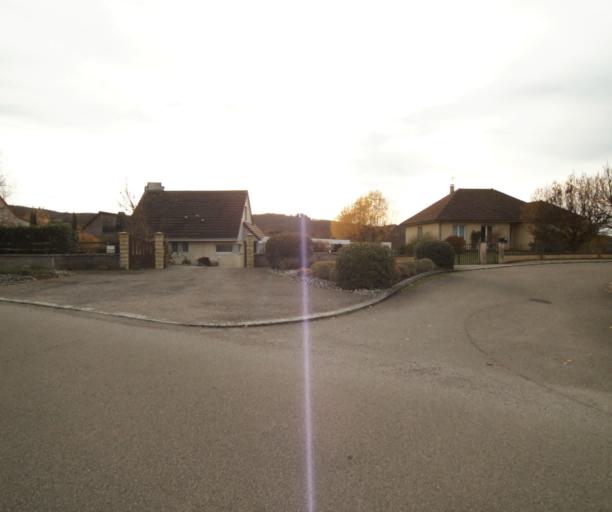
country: FR
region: Limousin
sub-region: Departement de la Correze
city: Sainte-Fortunade
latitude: 45.2151
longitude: 1.7678
